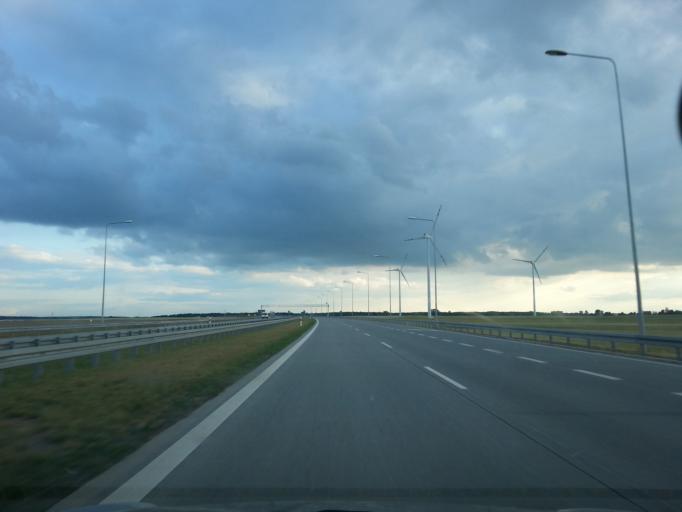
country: PL
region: Lodz Voivodeship
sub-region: Powiat sieradzki
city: Sieradz
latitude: 51.5553
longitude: 18.7148
